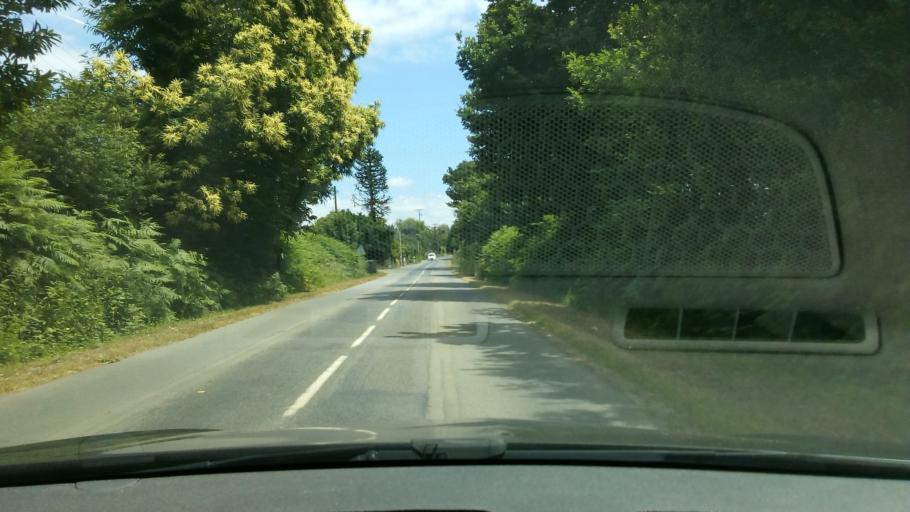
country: FR
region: Brittany
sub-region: Departement du Finistere
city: Tregunc
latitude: 47.8789
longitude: -3.8660
